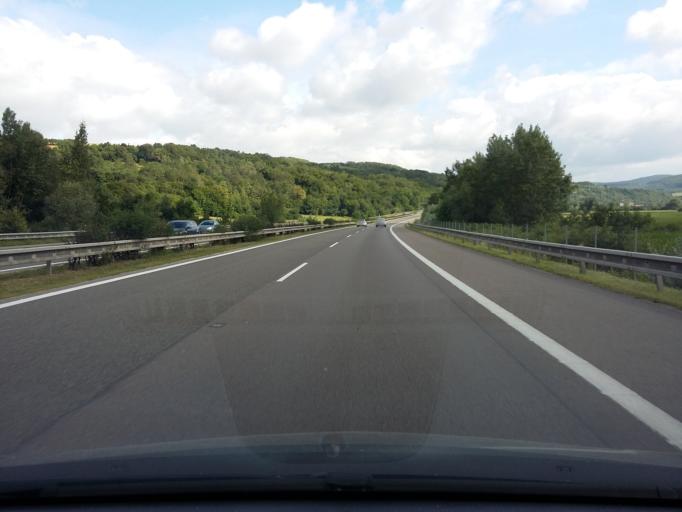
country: SK
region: Trenciansky
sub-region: Okres Trencin
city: Trencin
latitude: 48.8900
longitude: 17.9817
